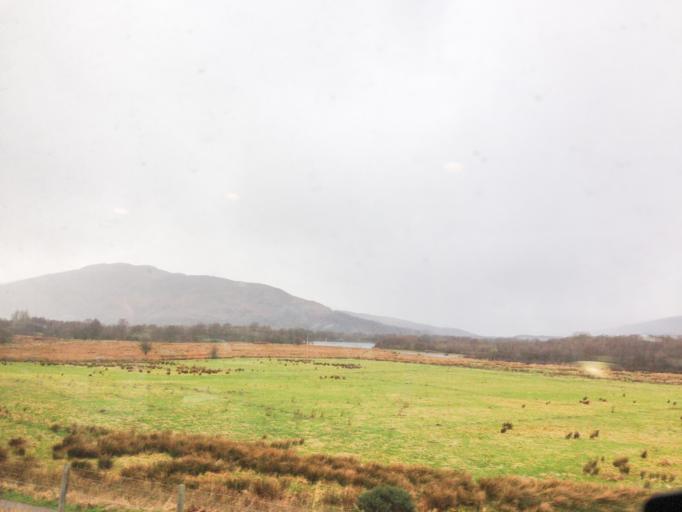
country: GB
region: Scotland
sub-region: Highland
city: Fort William
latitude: 56.8299
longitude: -5.0856
